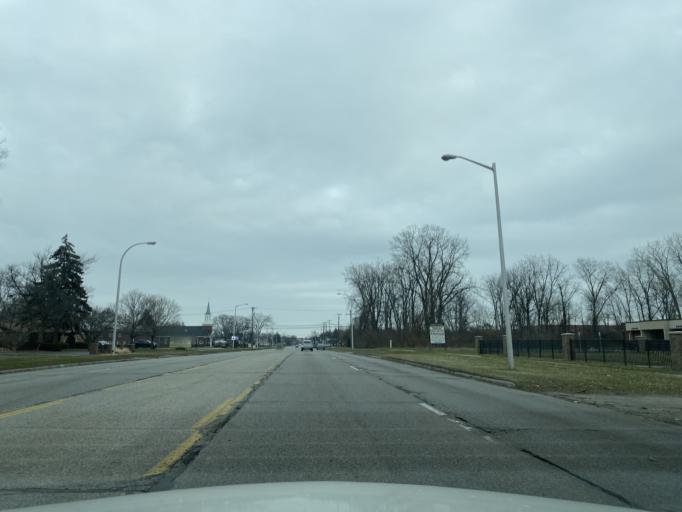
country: US
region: Michigan
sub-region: Wayne County
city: Taylor
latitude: 42.2263
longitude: -83.2743
